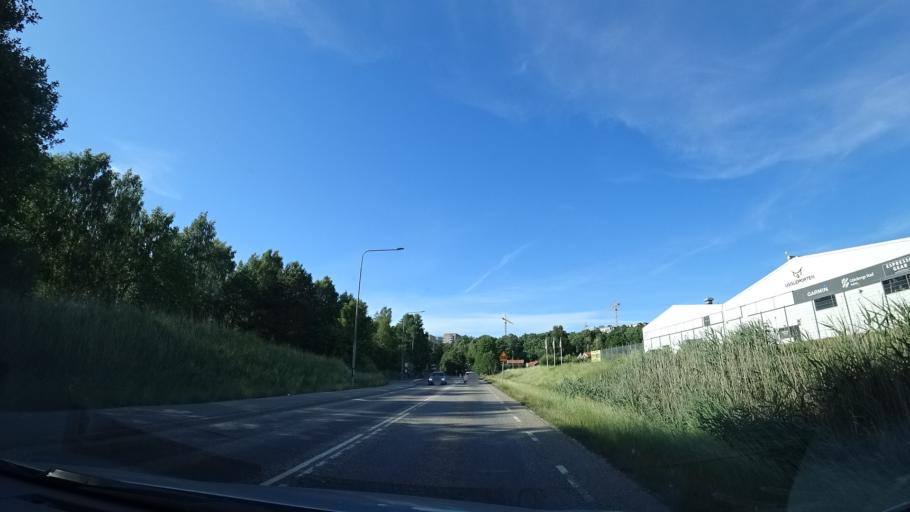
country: SE
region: Vaestra Goetaland
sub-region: Goteborg
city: Billdal
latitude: 57.5921
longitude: 11.9495
